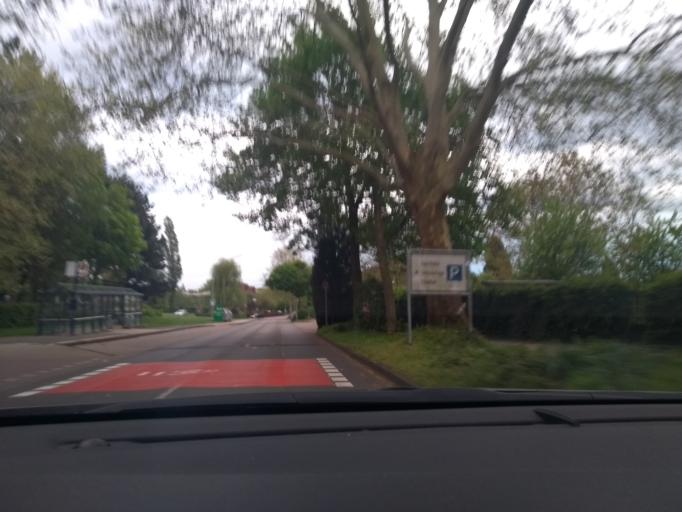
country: DE
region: North Rhine-Westphalia
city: Selm
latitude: 51.6634
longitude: 7.4670
